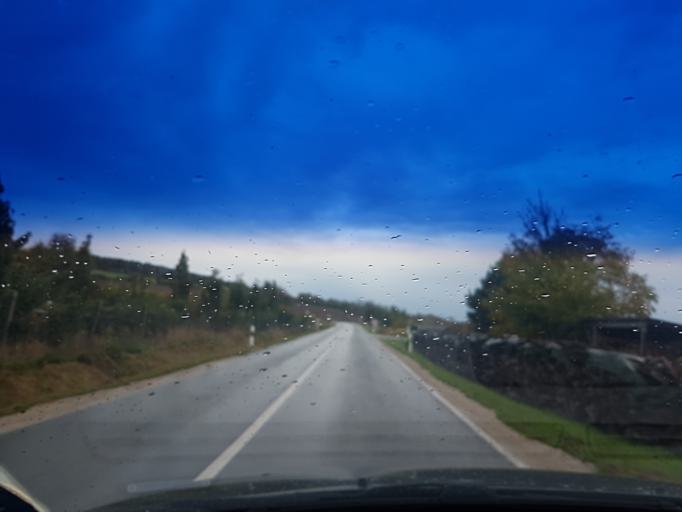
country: DE
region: Bavaria
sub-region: Regierungsbezirk Mittelfranken
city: Muhlhausen
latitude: 49.7574
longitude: 10.7837
